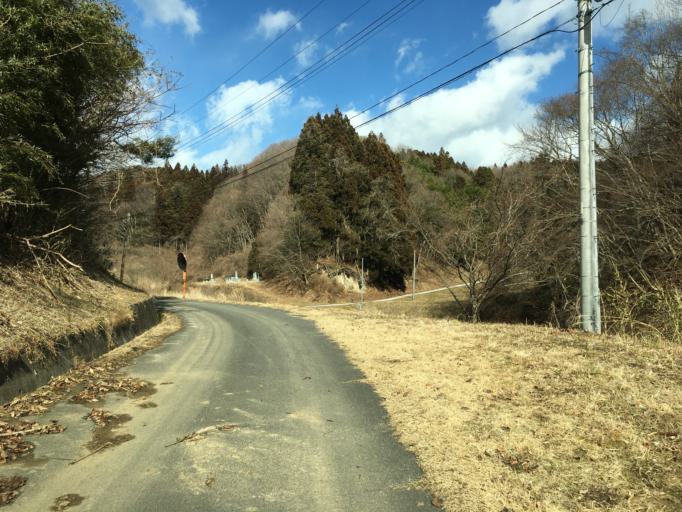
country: JP
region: Fukushima
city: Ishikawa
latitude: 37.2500
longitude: 140.5980
